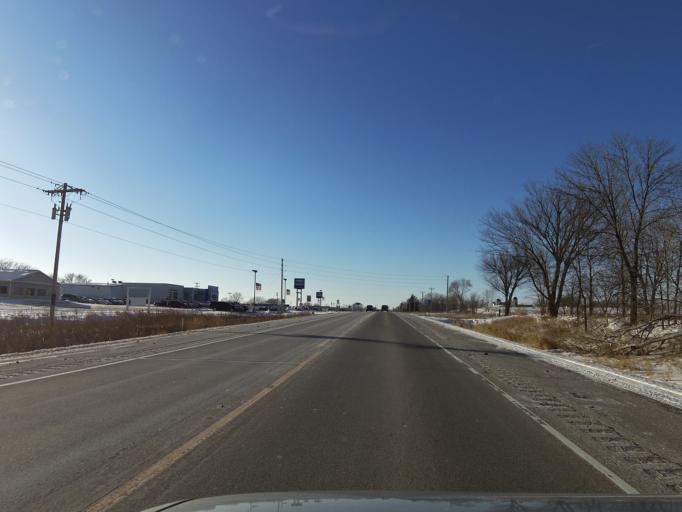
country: US
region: Minnesota
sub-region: Le Sueur County
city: New Prague
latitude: 44.5436
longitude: -93.5413
